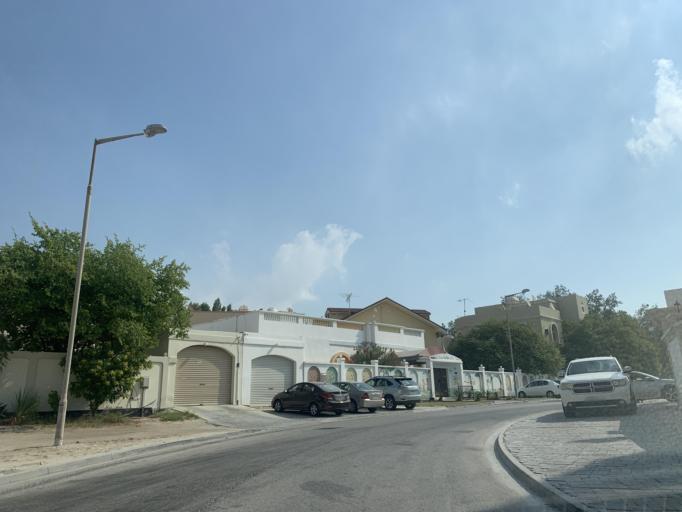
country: BH
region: Central Governorate
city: Madinat Hamad
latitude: 26.1067
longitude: 50.5032
